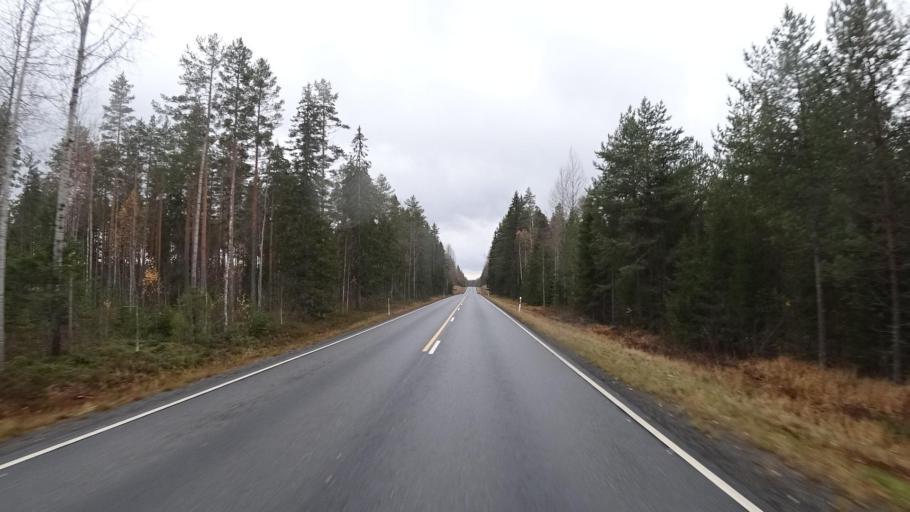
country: FI
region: Southern Savonia
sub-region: Mikkeli
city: Kangasniemi
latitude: 62.1580
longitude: 26.8257
